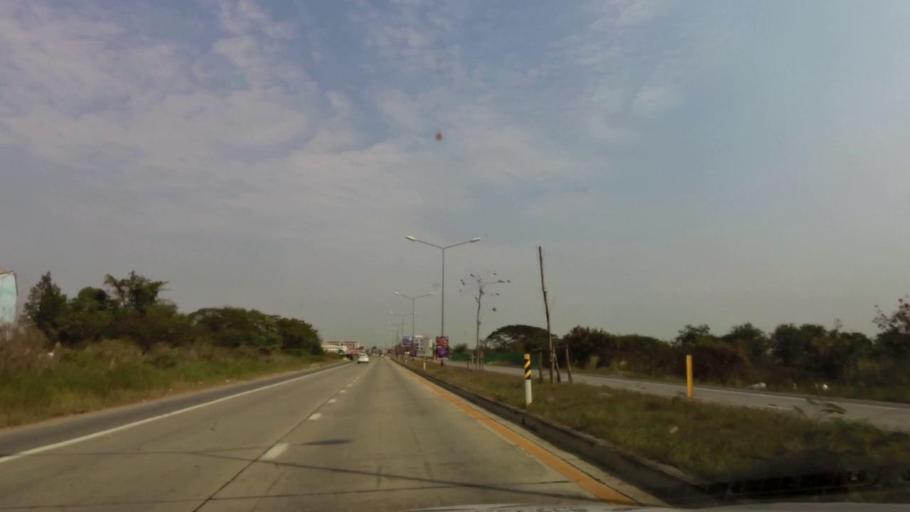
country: TH
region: Phra Nakhon Si Ayutthaya
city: Phra Nakhon Si Ayutthaya
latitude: 14.3332
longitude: 100.5994
